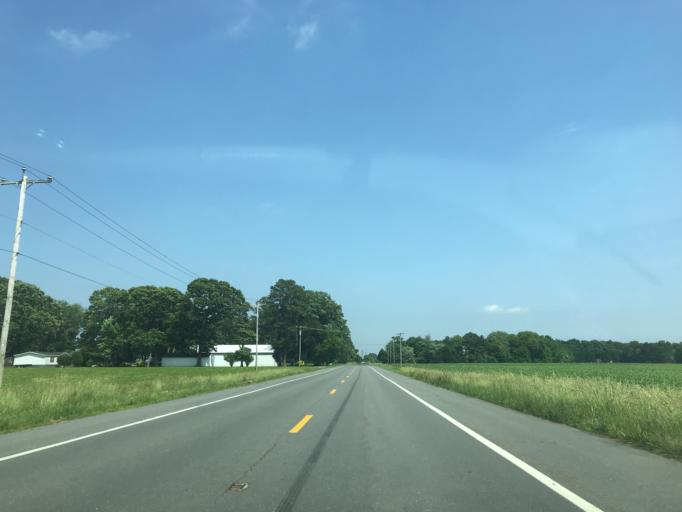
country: US
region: Maryland
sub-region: Dorchester County
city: Hurlock
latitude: 38.5918
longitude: -75.8827
